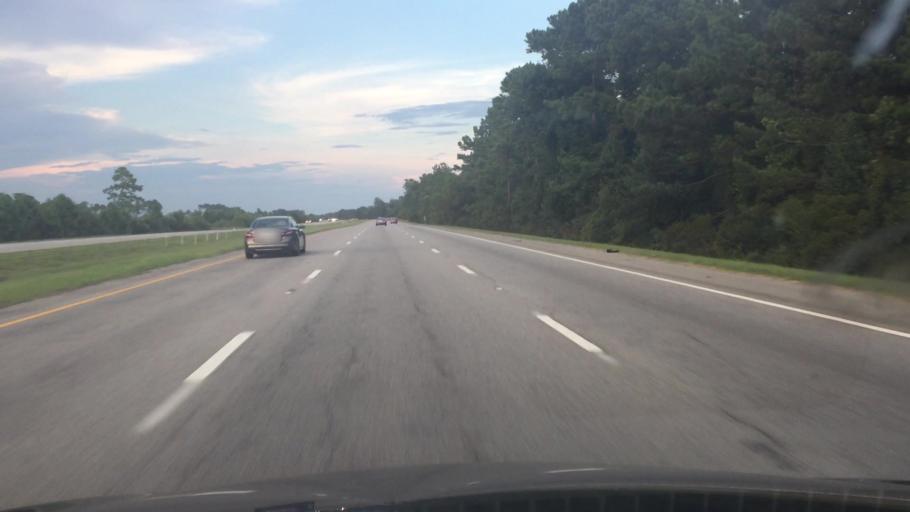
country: US
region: South Carolina
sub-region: Horry County
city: Myrtle Beach
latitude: 33.7680
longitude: -78.8286
